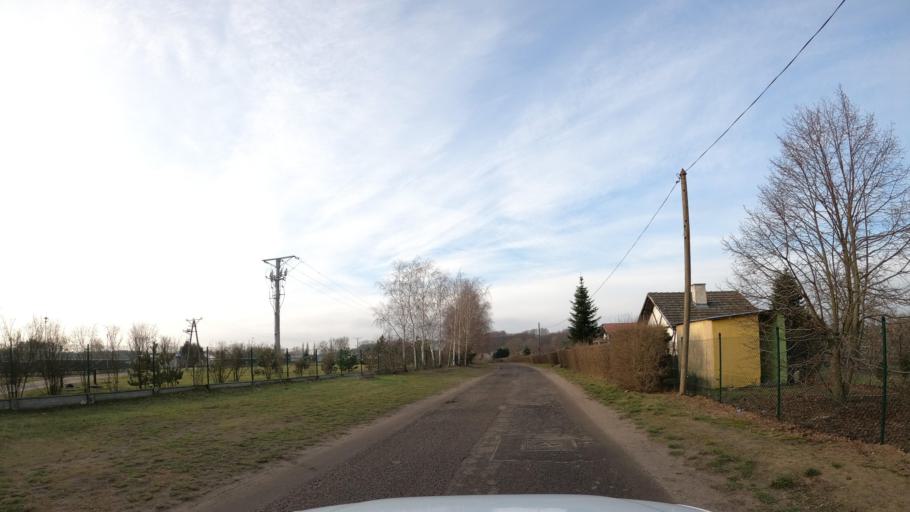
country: PL
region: West Pomeranian Voivodeship
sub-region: Powiat goleniowski
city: Goleniow
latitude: 53.5660
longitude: 14.8143
